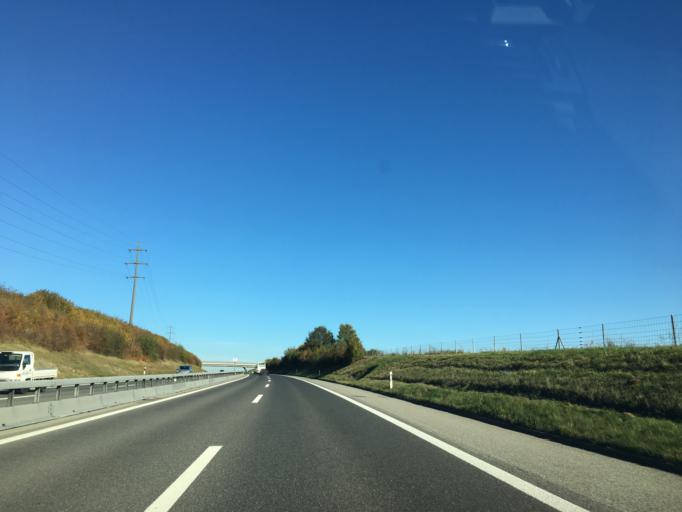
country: CH
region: Fribourg
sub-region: Sense District
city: Schmitten
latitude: 46.8711
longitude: 7.2492
